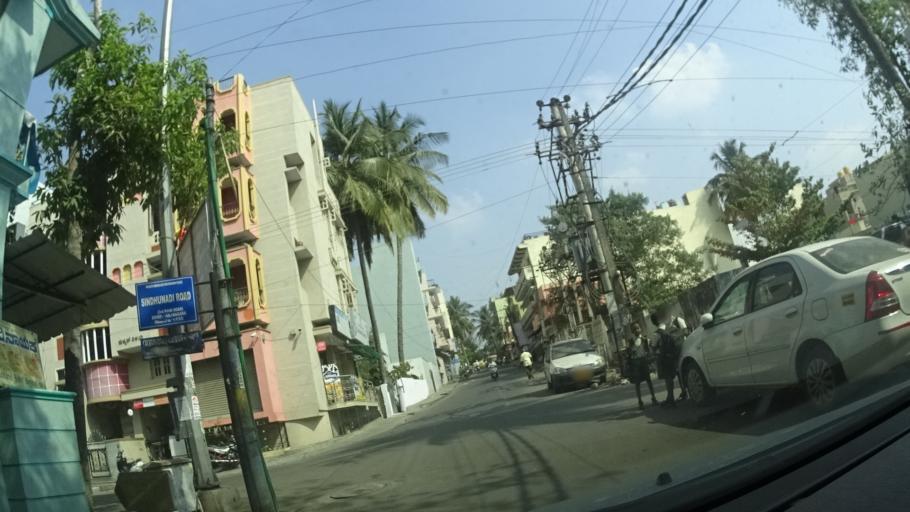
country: IN
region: Karnataka
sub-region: Bangalore Urban
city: Bangalore
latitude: 12.9487
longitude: 77.5564
